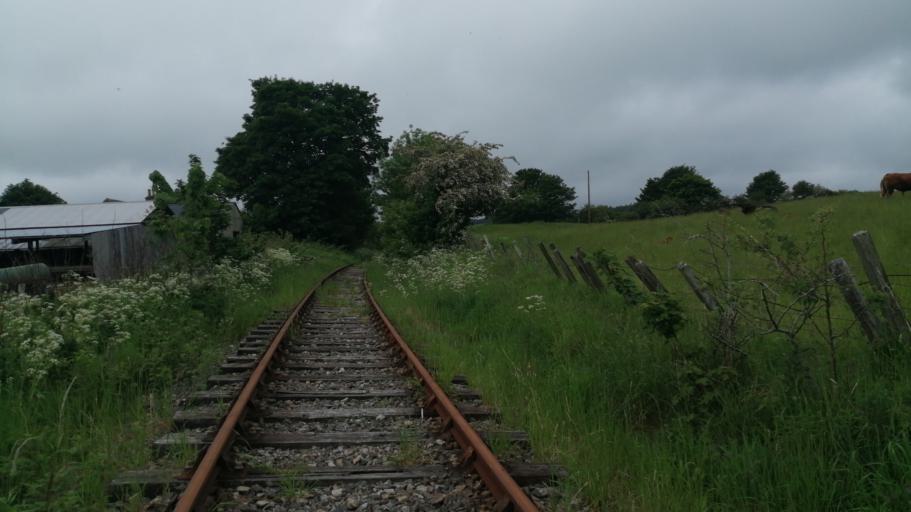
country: GB
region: Scotland
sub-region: Moray
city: Keith
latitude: 57.5336
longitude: -2.9655
